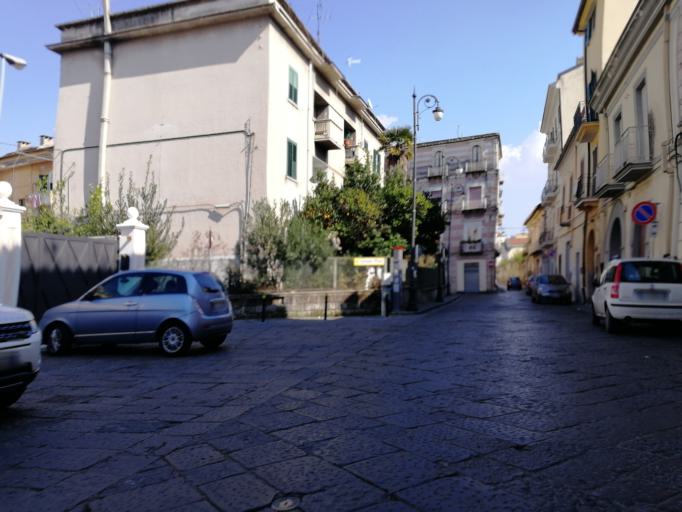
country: IT
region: Campania
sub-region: Provincia di Caserta
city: Santa Maria Capua Vetere
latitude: 41.0805
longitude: 14.2581
